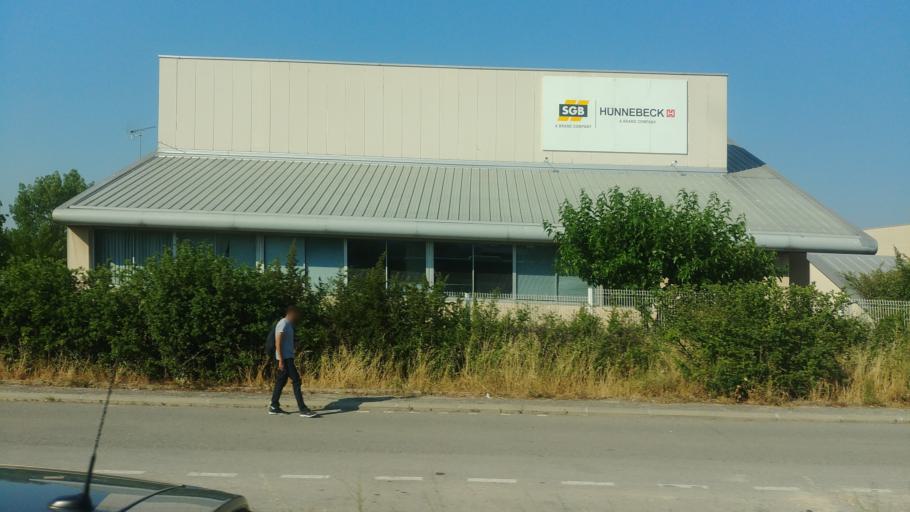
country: FR
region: Provence-Alpes-Cote d'Azur
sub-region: Departement des Bouches-du-Rhone
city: Cabries
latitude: 43.4830
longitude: 5.3841
